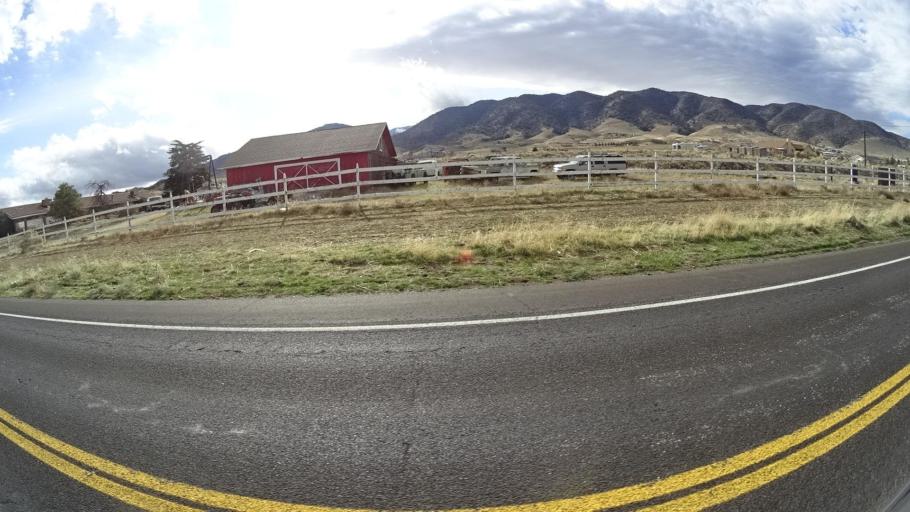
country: US
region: California
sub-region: Kern County
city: Tehachapi
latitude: 35.1093
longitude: -118.4535
